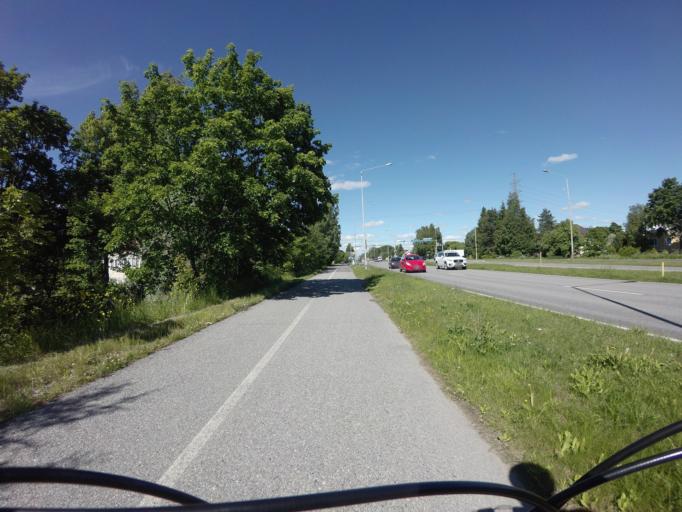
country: FI
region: Varsinais-Suomi
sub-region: Turku
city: Turku
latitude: 60.4745
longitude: 22.2651
